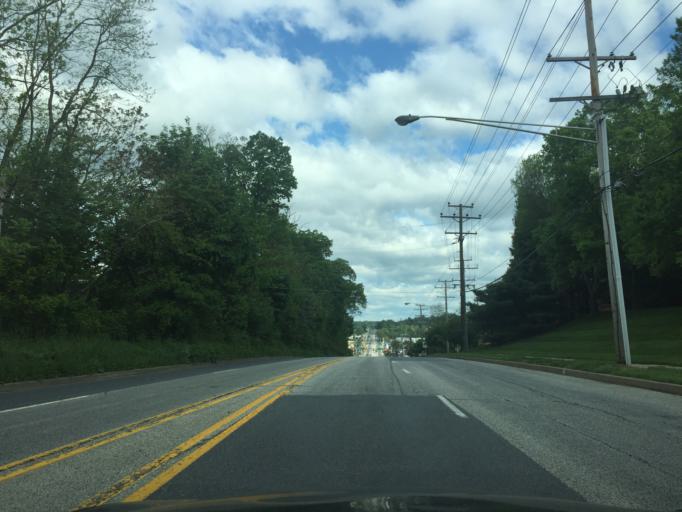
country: US
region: Maryland
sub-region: Baltimore County
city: Garrison
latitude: 39.4019
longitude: -76.7548
